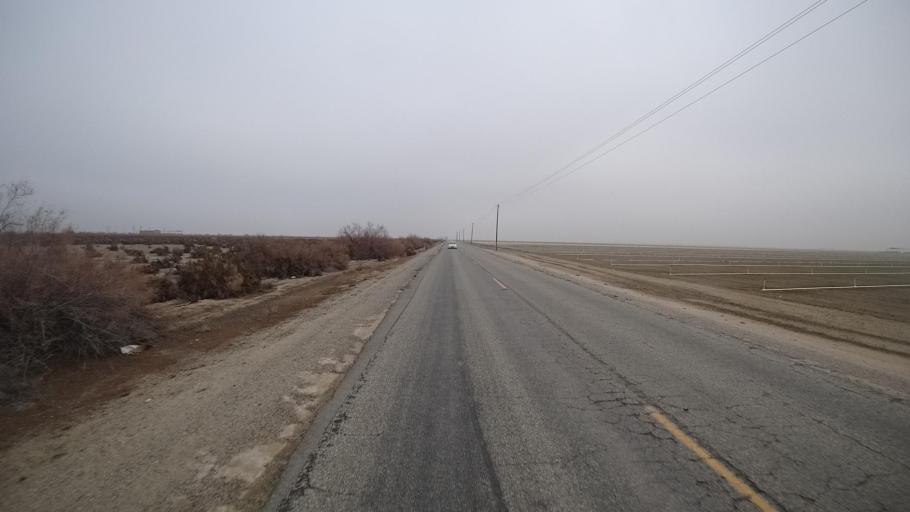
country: US
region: California
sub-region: Kern County
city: Maricopa
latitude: 35.1519
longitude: -119.2217
